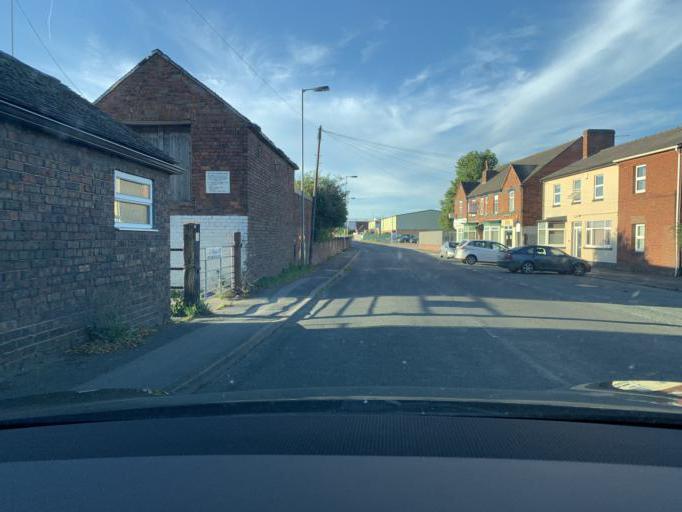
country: GB
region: England
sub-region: Staffordshire
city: Stafford
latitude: 52.8217
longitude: -2.1180
